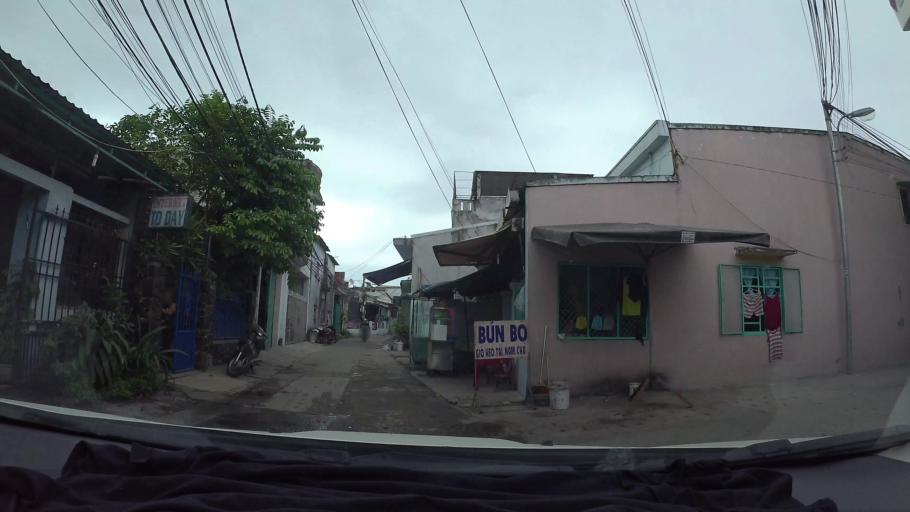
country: VN
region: Da Nang
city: Lien Chieu
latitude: 16.0525
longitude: 108.1577
